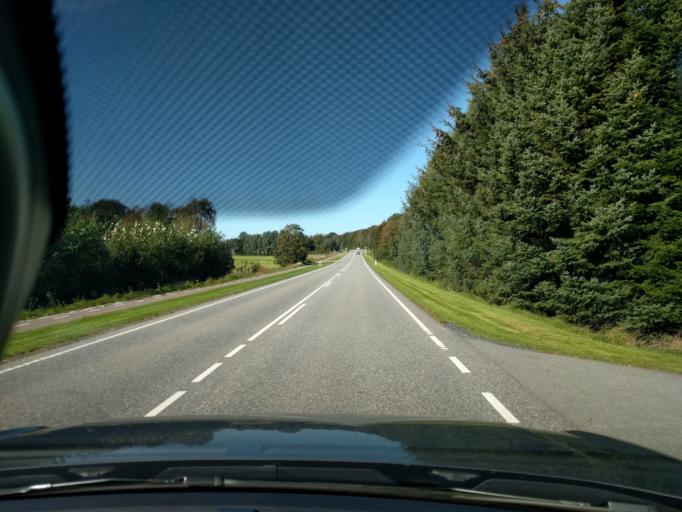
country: DK
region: North Denmark
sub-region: Vesthimmerland Kommune
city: Alestrup
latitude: 56.6989
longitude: 9.6460
